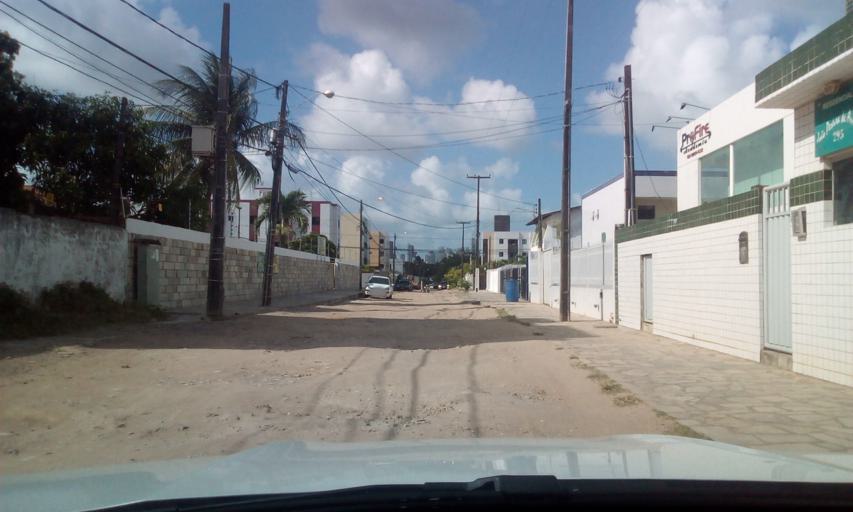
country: BR
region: Paraiba
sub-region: Joao Pessoa
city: Joao Pessoa
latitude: -7.1558
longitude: -34.8280
